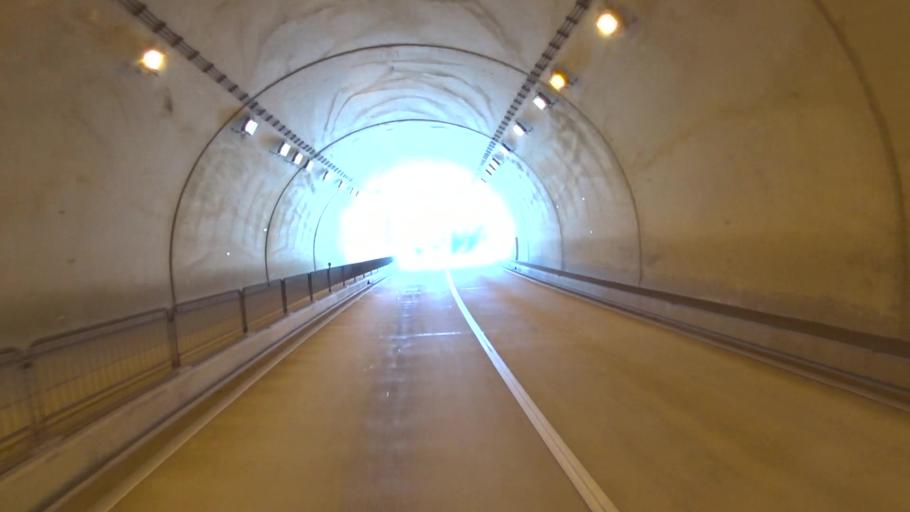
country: JP
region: Kyoto
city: Kameoka
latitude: 35.0744
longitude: 135.4722
